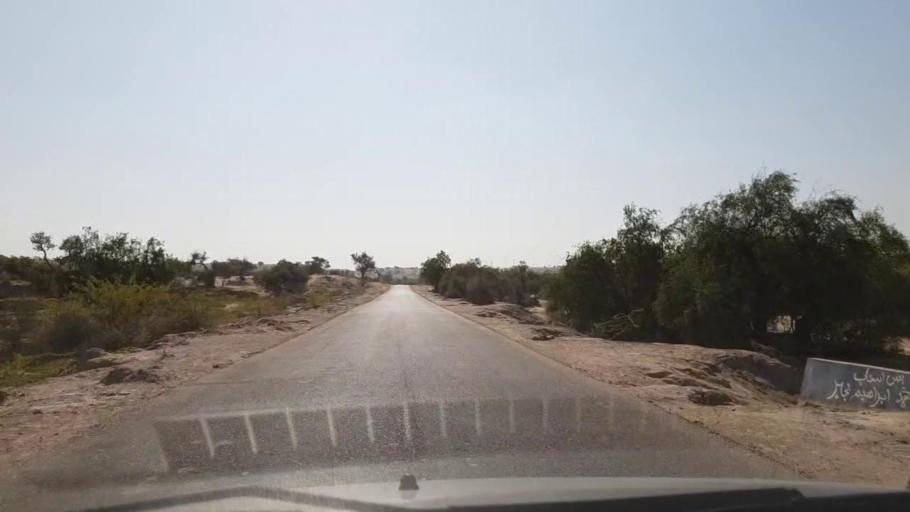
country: PK
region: Sindh
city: Mithi
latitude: 24.5999
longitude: 69.7149
